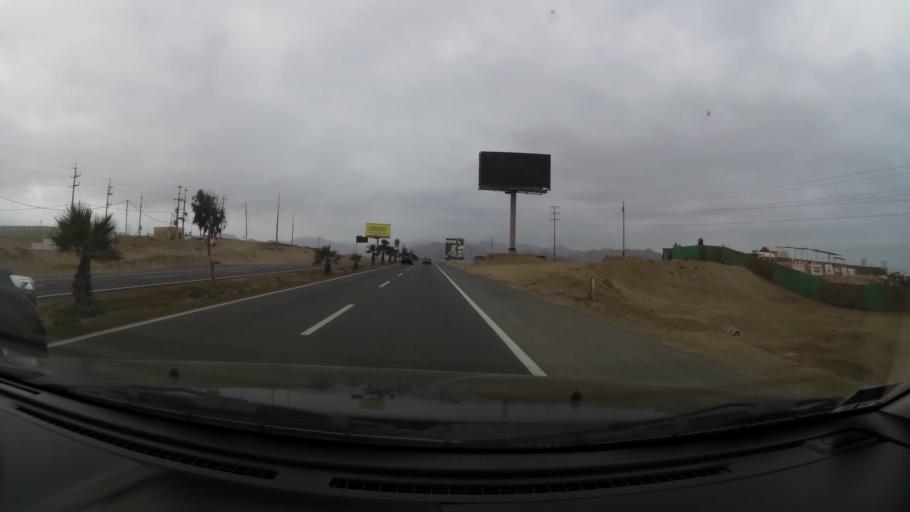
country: PE
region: Lima
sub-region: Lima
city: San Bartolo
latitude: -12.3790
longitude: -76.7768
